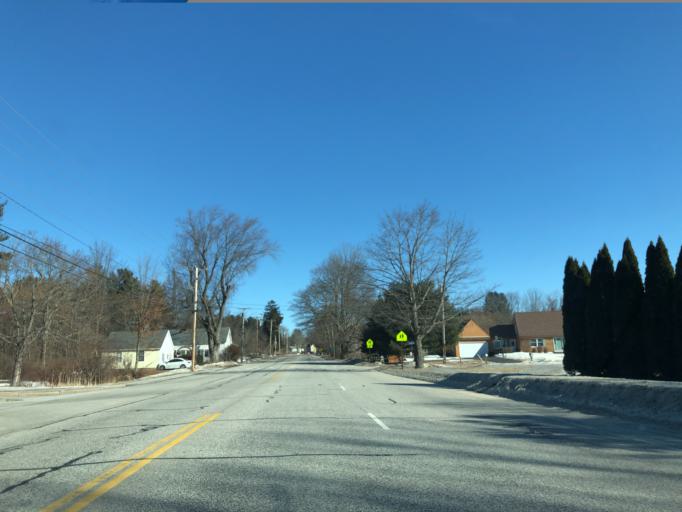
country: US
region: Maine
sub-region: Cumberland County
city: South Windham
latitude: 43.7866
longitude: -70.4113
